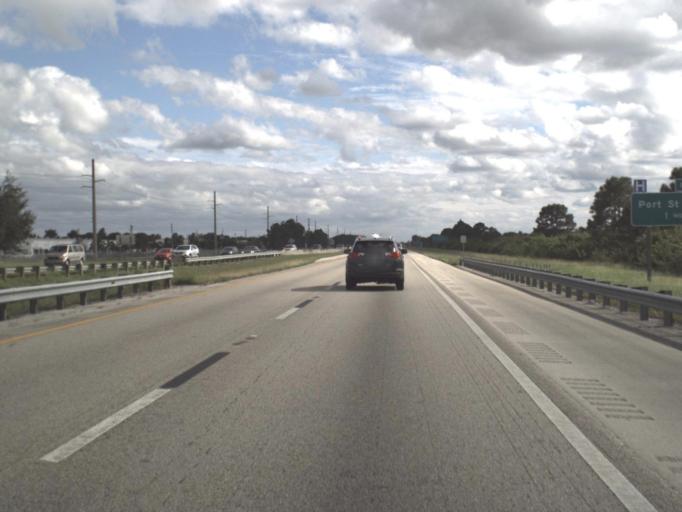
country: US
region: Florida
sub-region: Saint Lucie County
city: Port Saint Lucie
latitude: 27.2938
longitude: -80.3699
